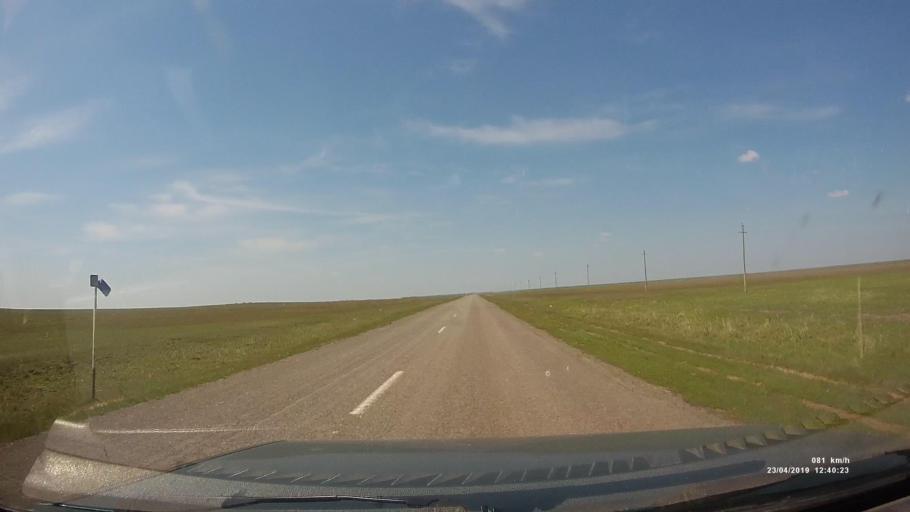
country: RU
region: Kalmykiya
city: Yashalta
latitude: 46.4400
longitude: 42.6973
